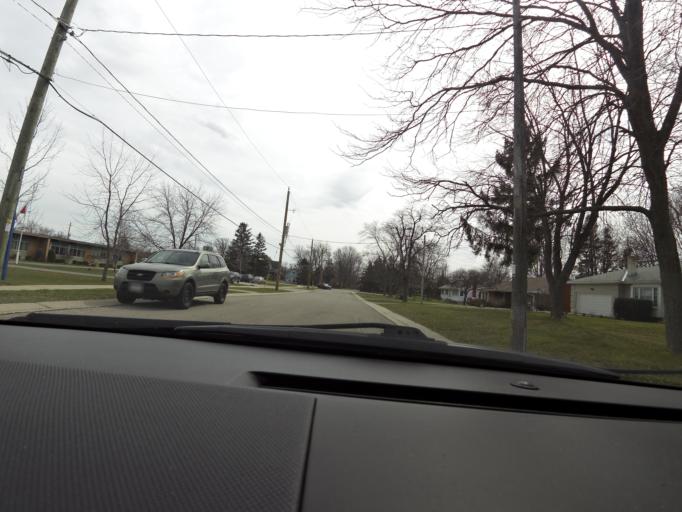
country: CA
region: Ontario
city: Ancaster
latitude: 42.9443
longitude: -79.8531
